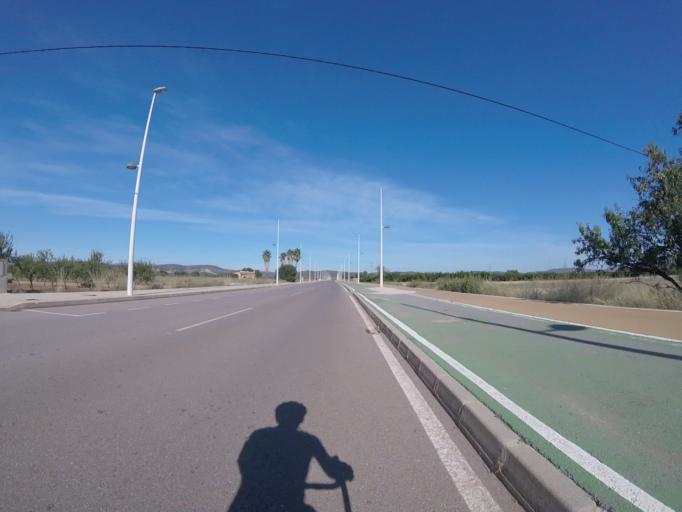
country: ES
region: Valencia
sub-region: Provincia de Castello
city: Torreblanca
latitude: 40.2124
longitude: 0.2234
